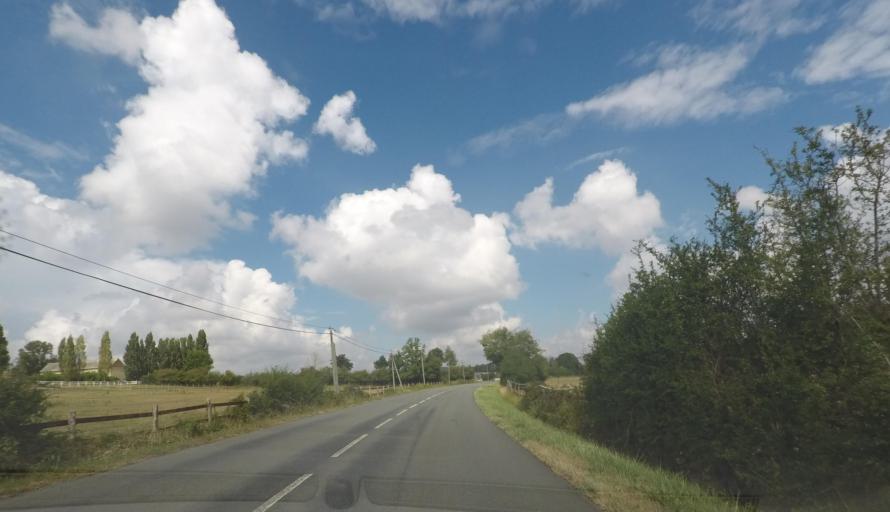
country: FR
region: Pays de la Loire
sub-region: Departement de la Sarthe
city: La Ferte-Bernard
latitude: 48.2657
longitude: 0.6002
